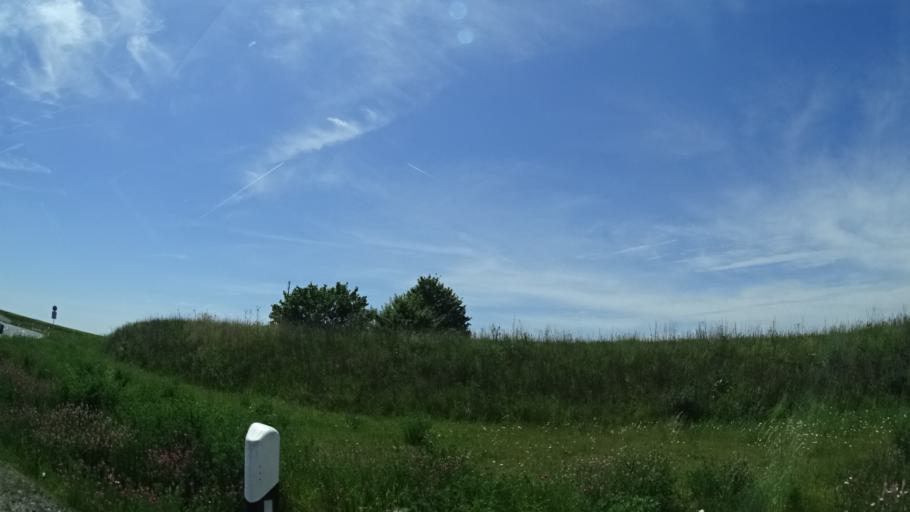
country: DE
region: Bavaria
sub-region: Regierungsbezirk Unterfranken
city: Oerlenbach
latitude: 50.1450
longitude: 10.1501
